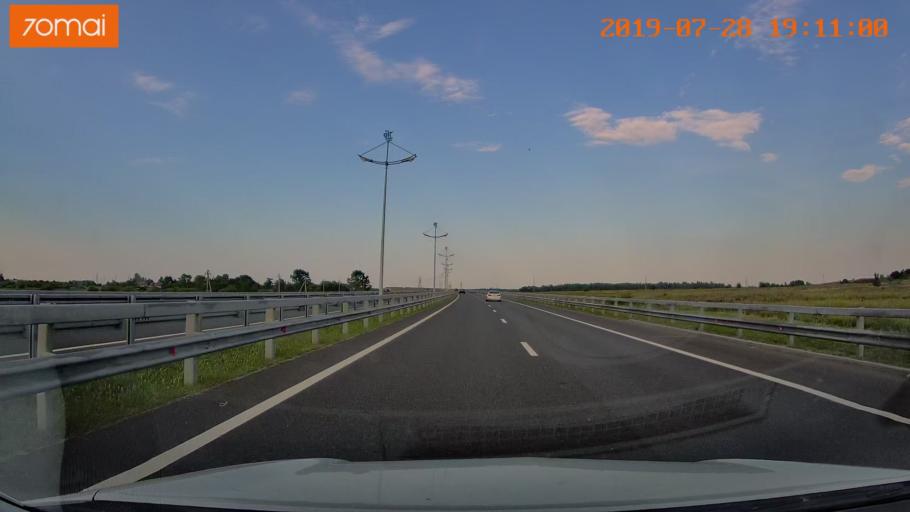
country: RU
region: Kaliningrad
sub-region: Gorod Kaliningrad
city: Pionerskiy
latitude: 54.9100
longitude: 20.2181
